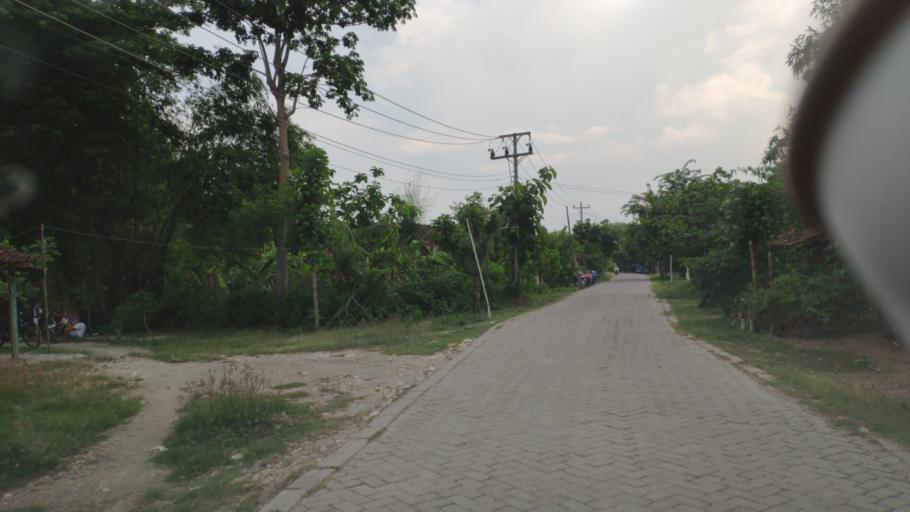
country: ID
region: Central Java
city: Pulo
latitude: -7.2050
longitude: 111.4961
